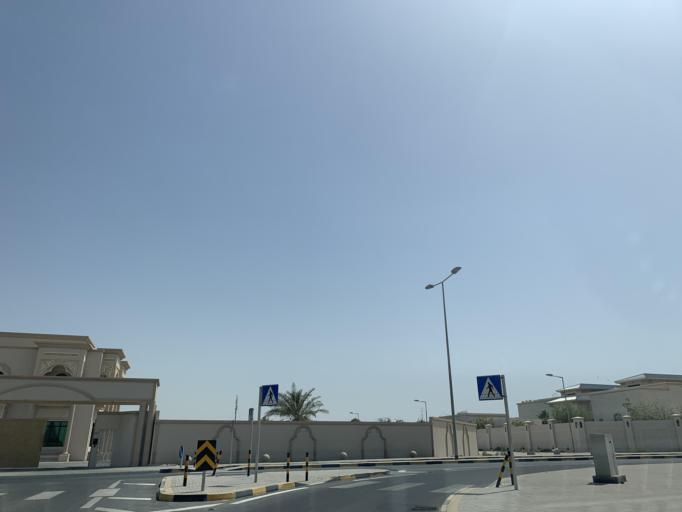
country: BH
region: Northern
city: Madinat `Isa
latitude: 26.1512
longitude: 50.5445
